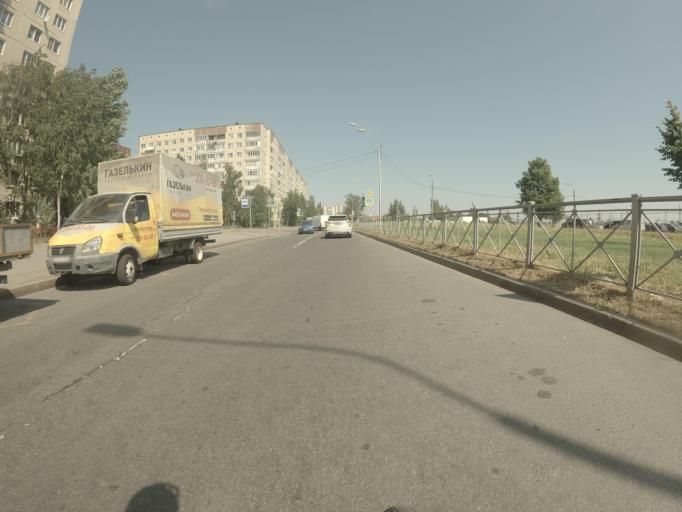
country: RU
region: St.-Petersburg
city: Krasnogvargeisky
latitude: 59.9390
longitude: 30.5014
